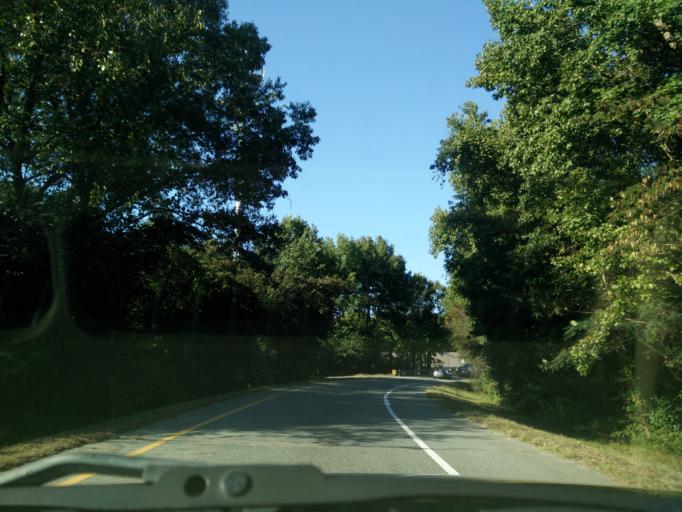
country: US
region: Virginia
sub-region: City of Chesapeake
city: Chesapeake
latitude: 36.7633
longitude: -76.2655
